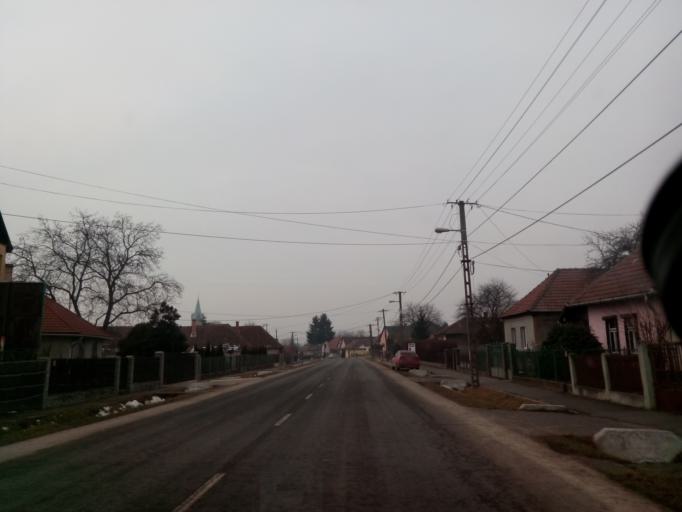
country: HU
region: Borsod-Abauj-Zemplen
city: Gonc
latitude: 48.5233
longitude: 21.2532
